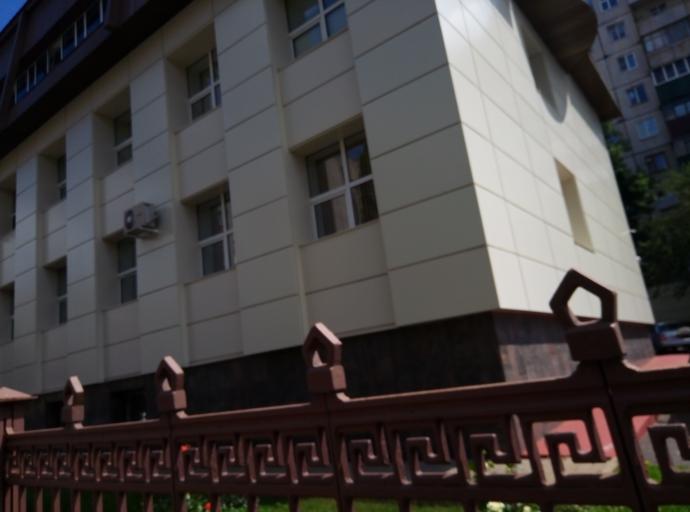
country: RU
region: Kursk
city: Kursk
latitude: 51.7383
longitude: 36.1874
